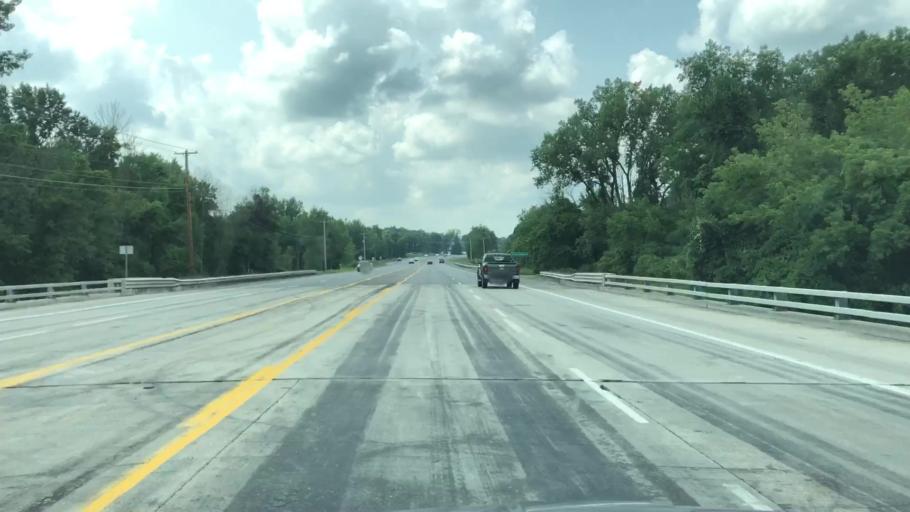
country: US
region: Michigan
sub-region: Midland County
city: Coleman
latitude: 43.6105
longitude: -84.5742
